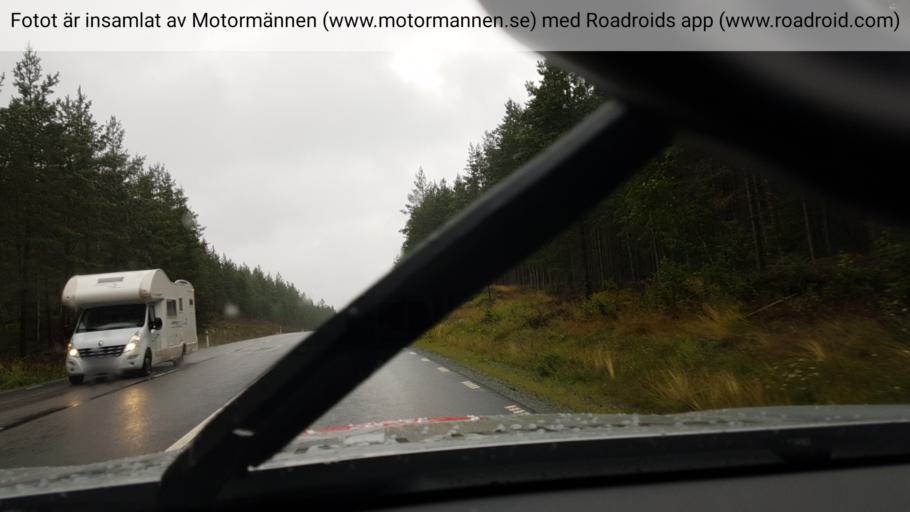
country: SE
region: Vaestra Goetaland
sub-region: Bengtsfors Kommun
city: Dals Langed
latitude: 58.8471
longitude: 12.1680
